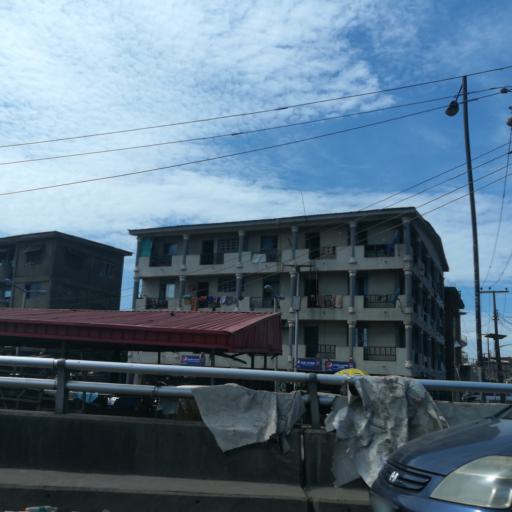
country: NG
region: Lagos
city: Lagos
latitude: 6.4658
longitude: 3.3900
